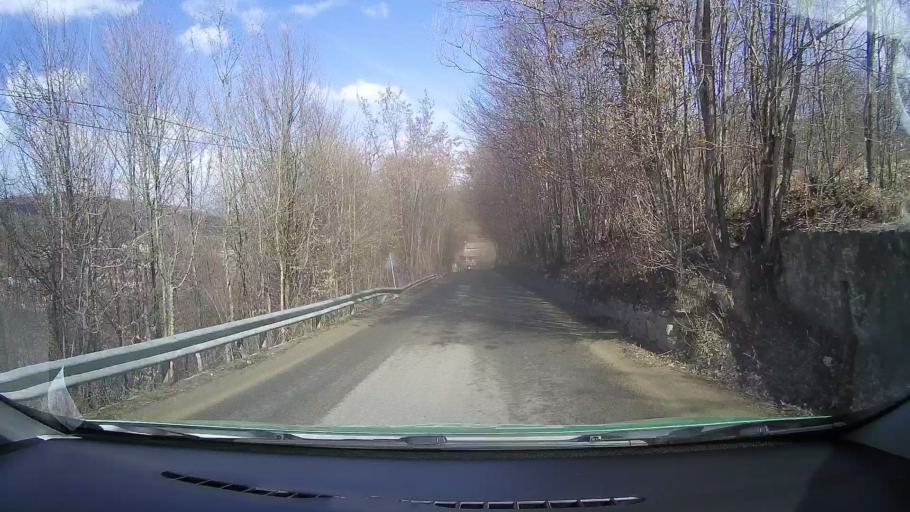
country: RO
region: Dambovita
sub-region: Comuna Runcu
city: Badeni
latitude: 45.1470
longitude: 25.4037
